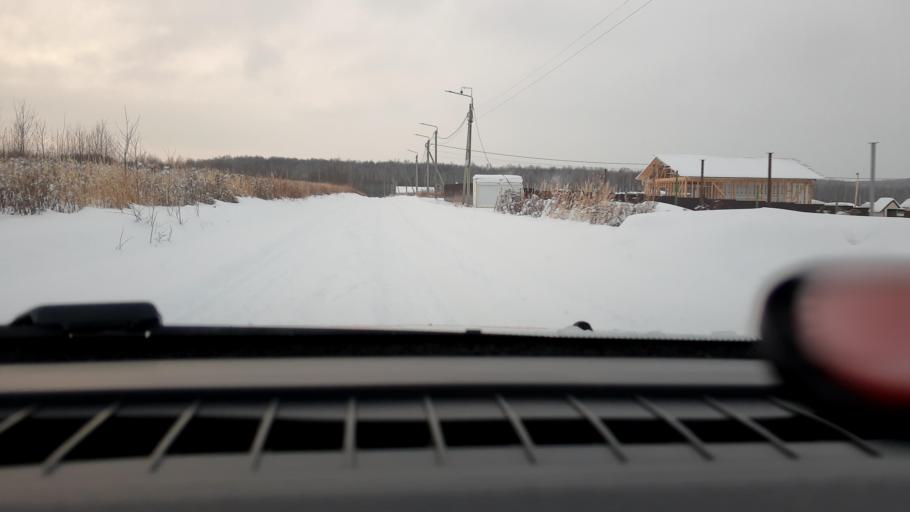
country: RU
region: Nizjnij Novgorod
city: Afonino
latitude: 56.1329
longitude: 43.9864
